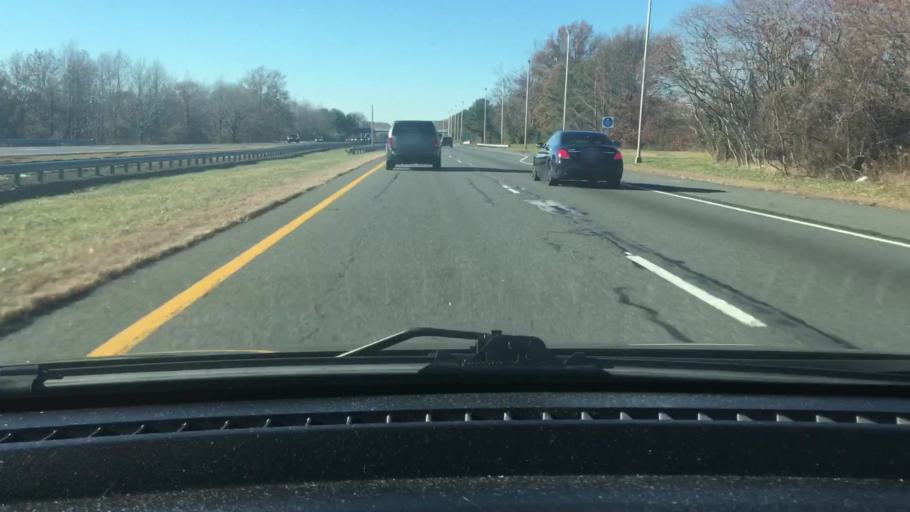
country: US
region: New Jersey
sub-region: Monmouth County
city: Allentown
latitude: 40.1842
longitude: -74.5650
